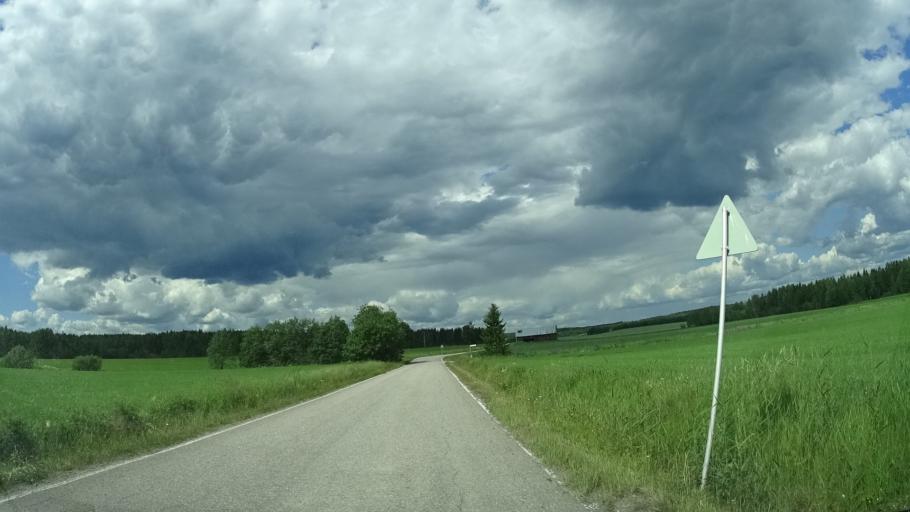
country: FI
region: Uusimaa
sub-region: Helsinki
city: Espoo
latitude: 60.4123
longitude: 24.5580
